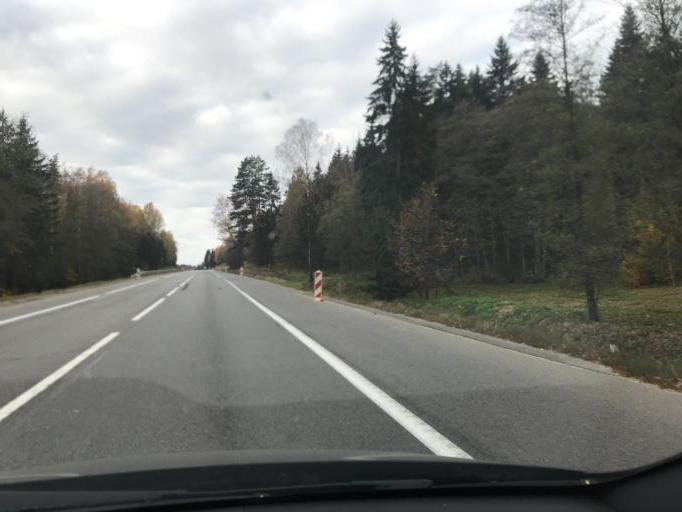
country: BY
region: Minsk
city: Astrashytski Haradok
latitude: 54.0577
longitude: 27.7294
